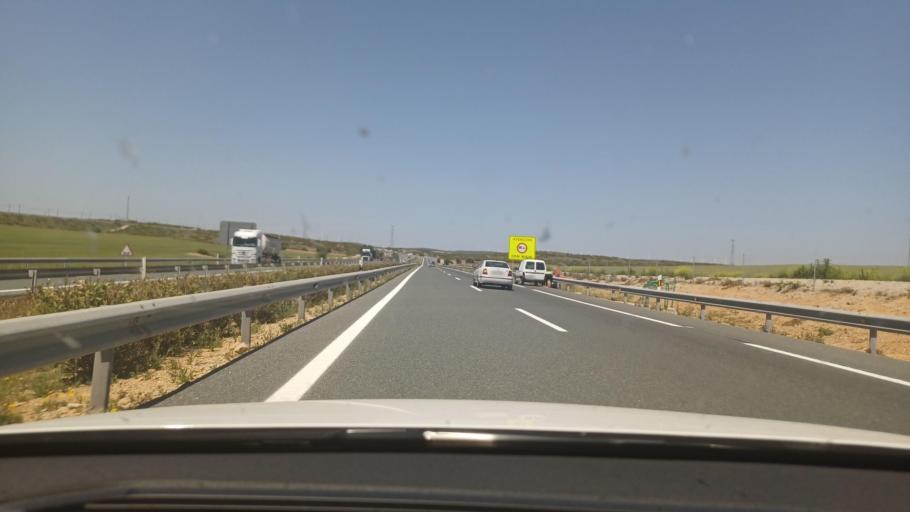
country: ES
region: Castille-La Mancha
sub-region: Provincia de Albacete
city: Alpera
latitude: 38.8786
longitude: -1.2378
